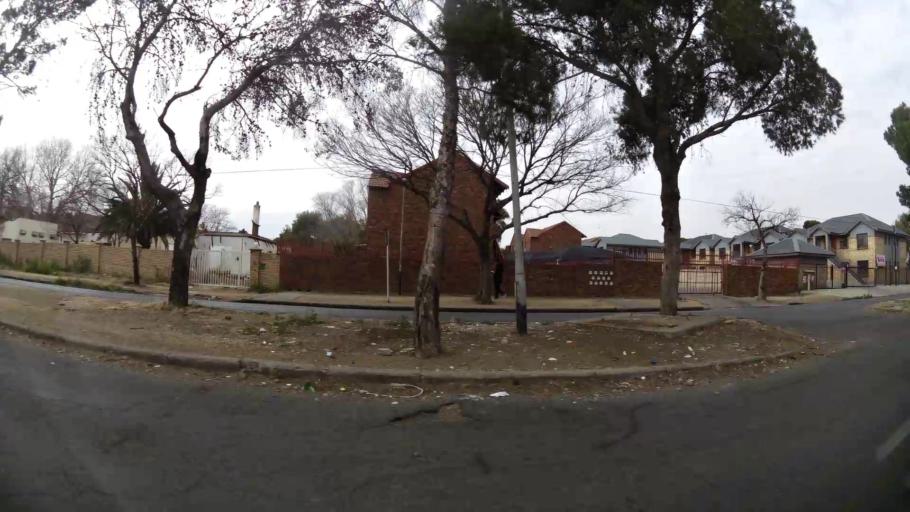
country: ZA
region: Orange Free State
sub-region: Mangaung Metropolitan Municipality
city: Bloemfontein
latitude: -29.1231
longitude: 26.2033
